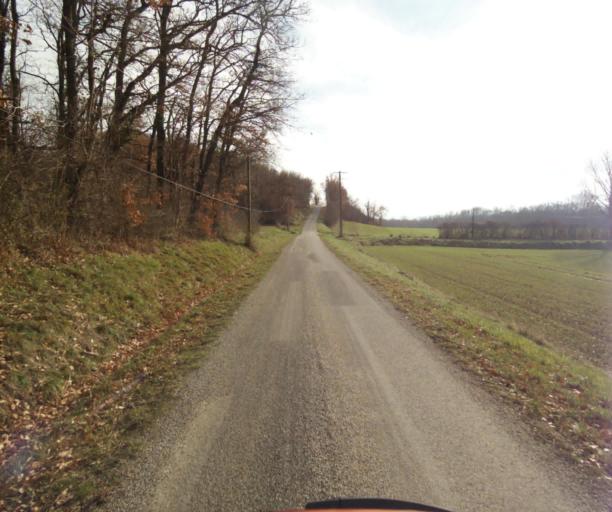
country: FR
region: Languedoc-Roussillon
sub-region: Departement de l'Aude
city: Belpech
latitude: 43.1700
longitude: 1.7378
